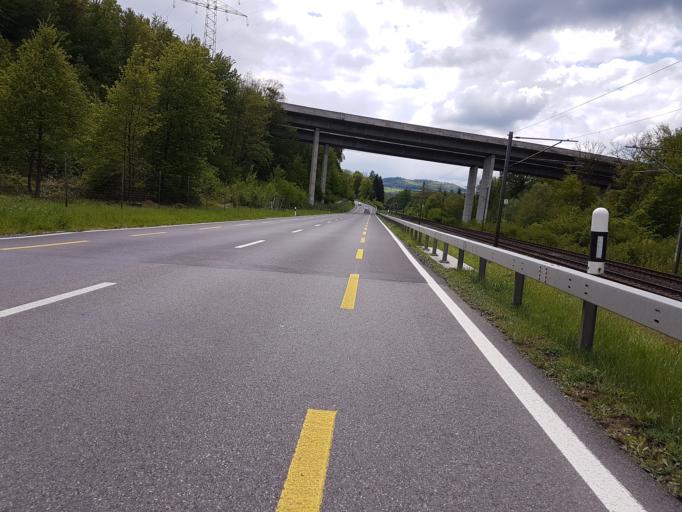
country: CH
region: Aargau
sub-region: Bezirk Brugg
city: Schinznach Bad
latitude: 47.4634
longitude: 8.1735
